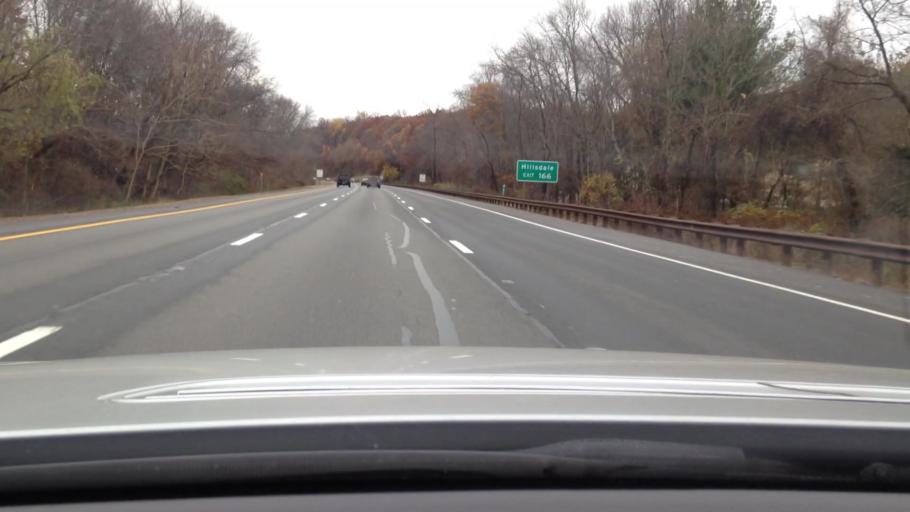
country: US
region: New Jersey
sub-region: Bergen County
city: Woodcliff Lake
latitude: 40.9959
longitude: -74.0727
